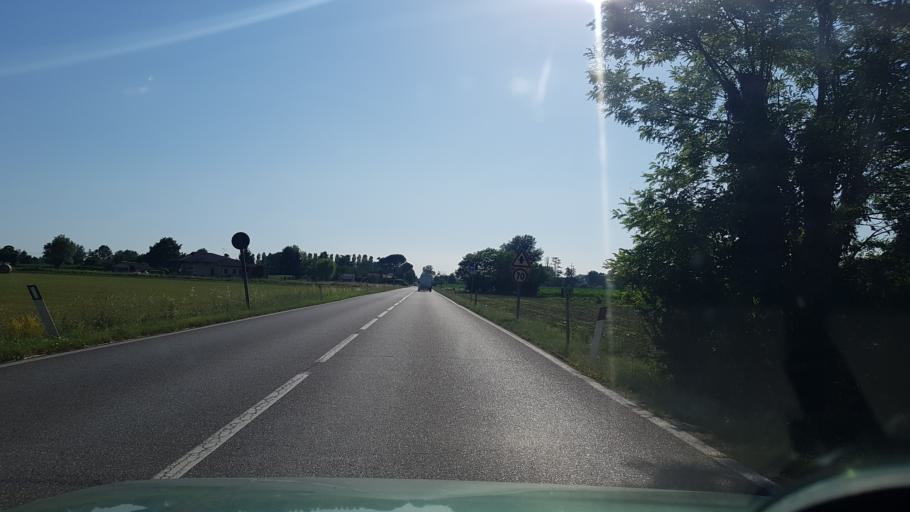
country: IT
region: Friuli Venezia Giulia
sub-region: Provincia di Udine
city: Ruda
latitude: 45.8387
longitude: 13.3841
